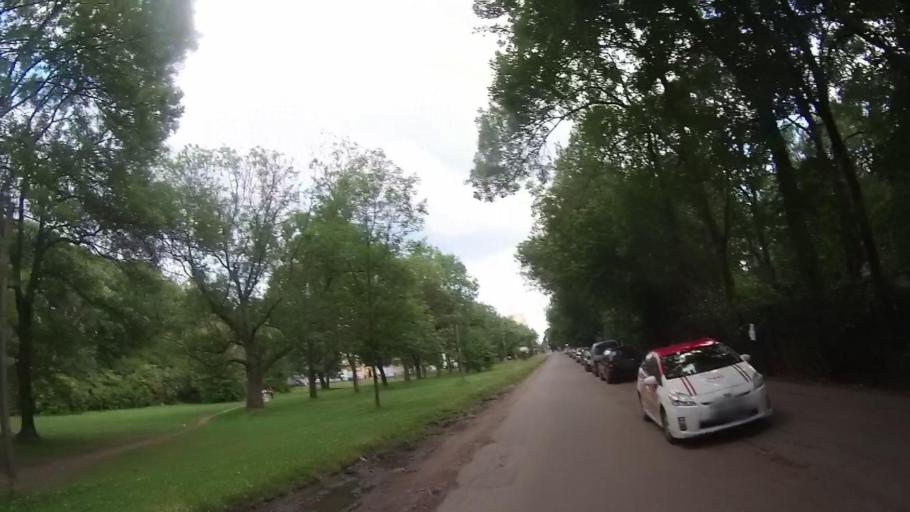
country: PL
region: Masovian Voivodeship
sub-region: Warszawa
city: Praga Poludnie
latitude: 52.2425
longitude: 21.0612
